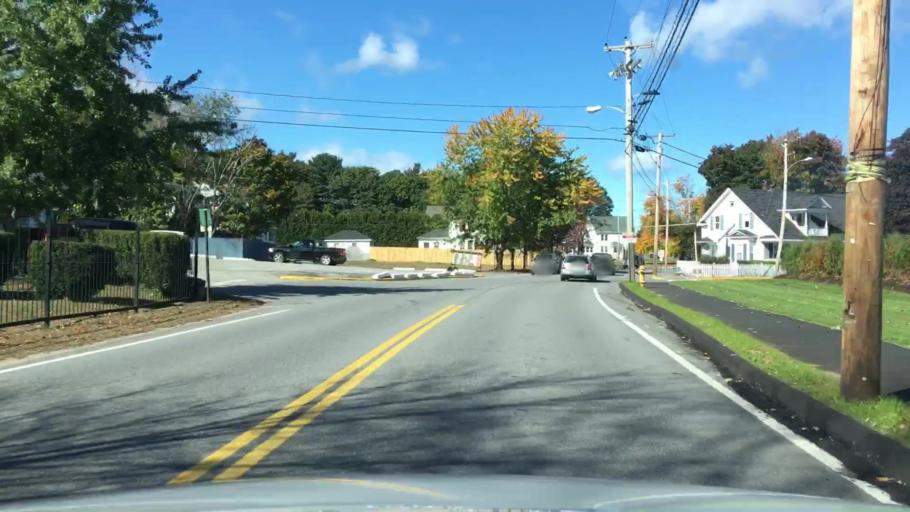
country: US
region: Maine
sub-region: York County
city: Biddeford
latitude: 43.4738
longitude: -70.4588
